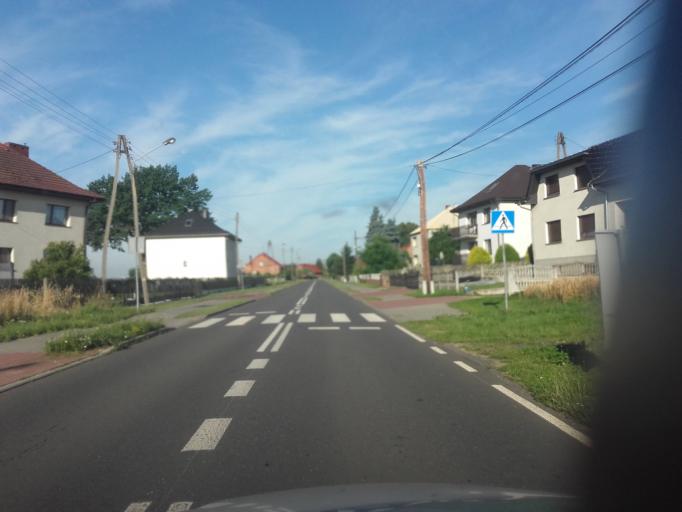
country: PL
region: Opole Voivodeship
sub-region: Powiat oleski
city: Olesno
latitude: 50.9315
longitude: 18.5247
